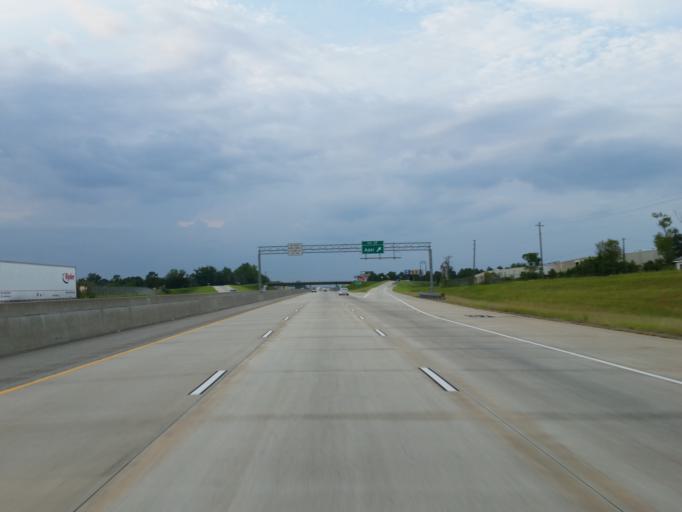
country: US
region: Georgia
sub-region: Cook County
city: Adel
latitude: 31.1087
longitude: -83.4256
